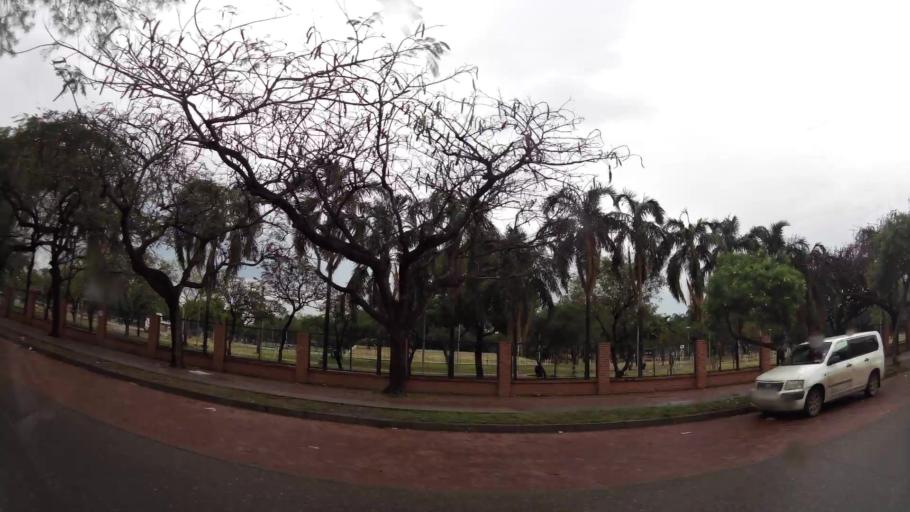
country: BO
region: Santa Cruz
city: Santa Cruz de la Sierra
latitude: -17.7934
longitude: -63.1681
